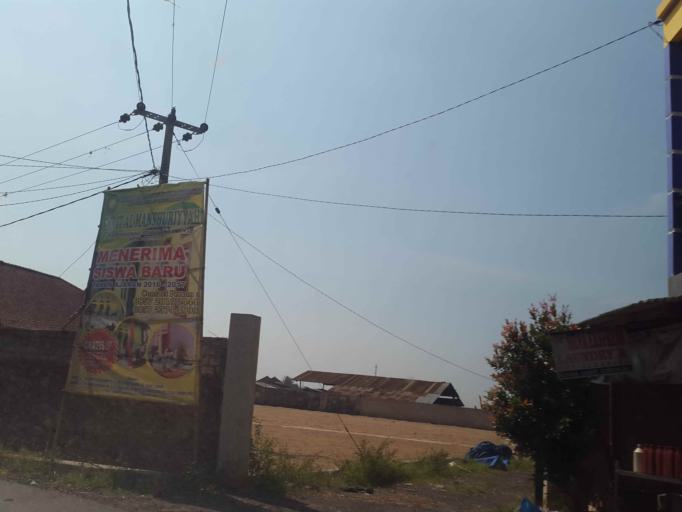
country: ID
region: West Java
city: Ciranjang-hilir
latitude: -6.8444
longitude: 107.1074
